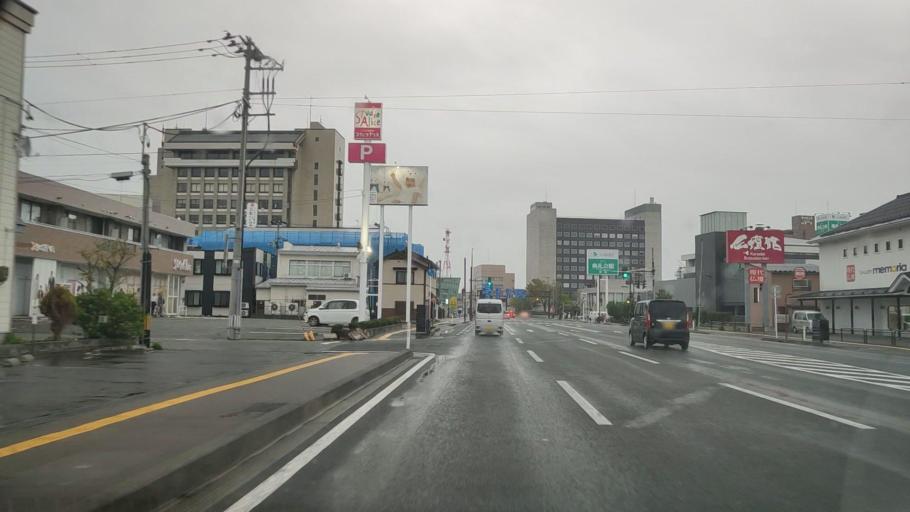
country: JP
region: Akita
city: Akita Shi
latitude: 39.7215
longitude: 140.1087
